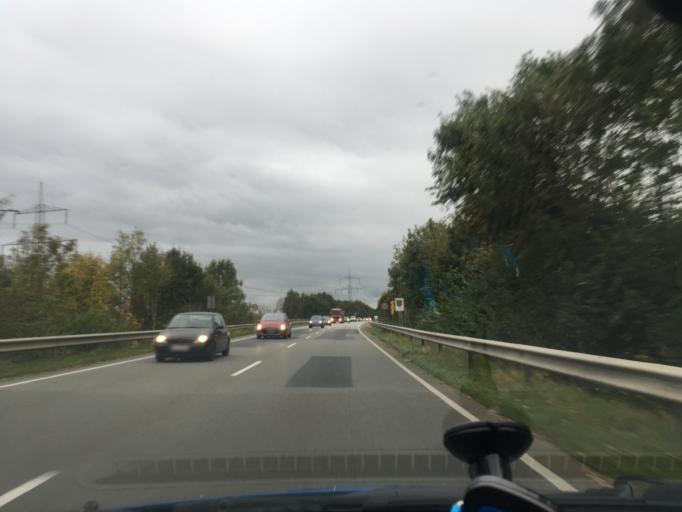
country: DE
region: Lower Saxony
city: Handorf
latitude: 53.3589
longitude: 10.3435
